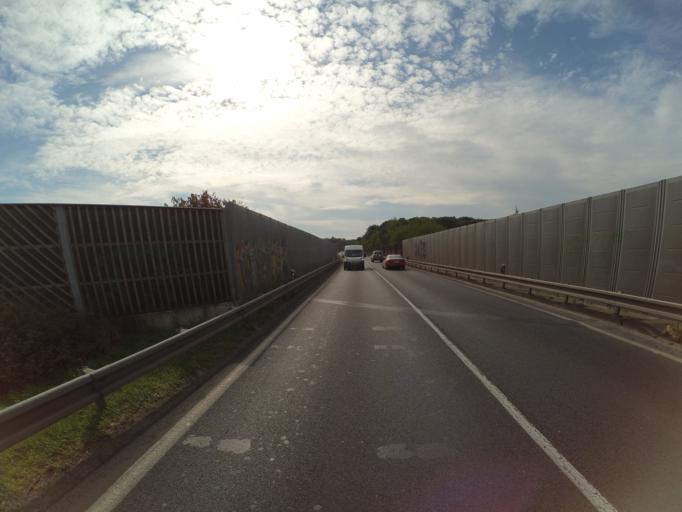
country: FR
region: Pays de la Loire
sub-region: Departement de Maine-et-Loire
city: Saumur
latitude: 47.2600
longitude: -0.0972
